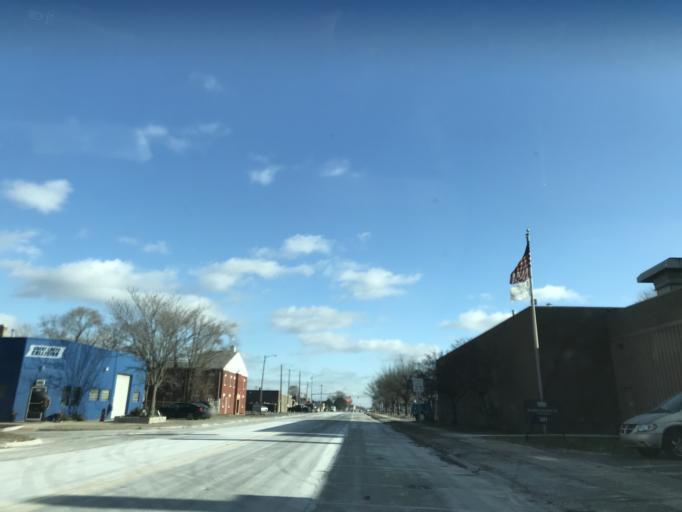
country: US
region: Michigan
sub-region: Oakland County
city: Madison Heights
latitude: 42.4760
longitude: -83.1075
